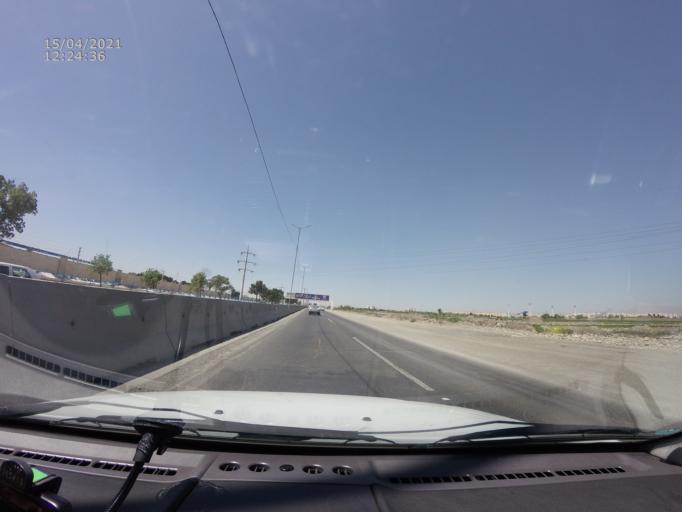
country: IR
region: Tehran
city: Eslamshahr
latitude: 35.5118
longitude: 51.2548
